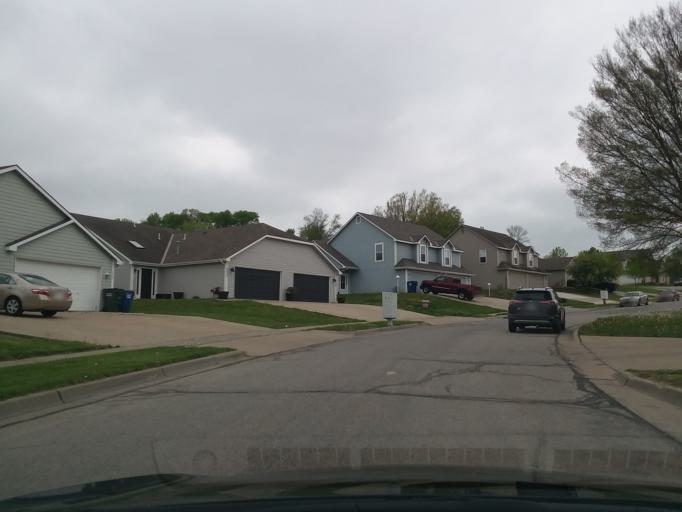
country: US
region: Kansas
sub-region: Douglas County
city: Lawrence
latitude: 38.9939
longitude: -95.2828
